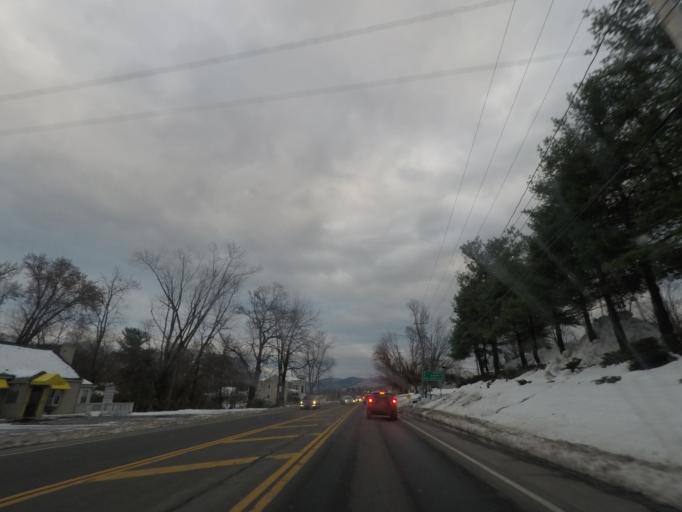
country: US
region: New York
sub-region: Orange County
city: Balmville
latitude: 41.5218
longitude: -74.0265
